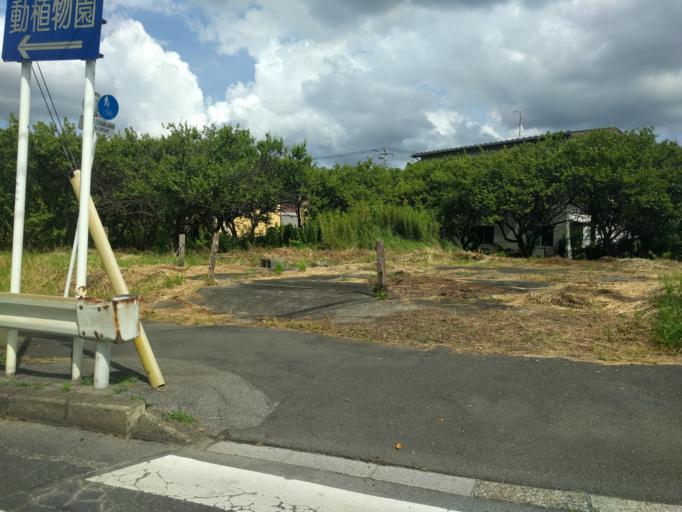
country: JP
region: Chiba
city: Funabashi
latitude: 35.7477
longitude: 139.9578
